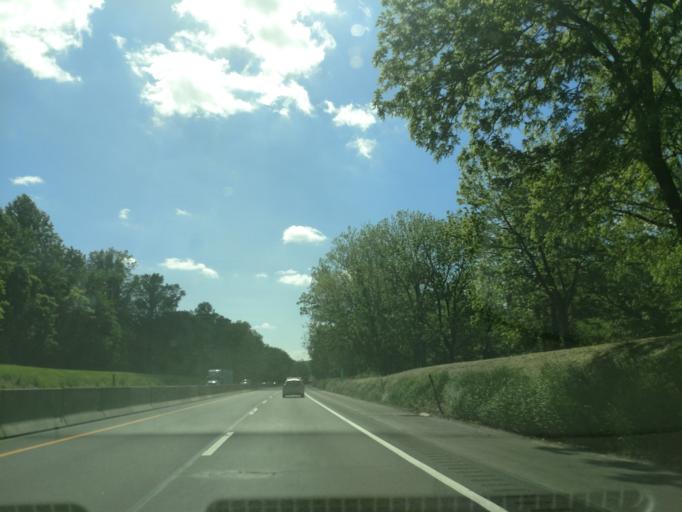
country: US
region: Pennsylvania
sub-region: Chester County
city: Chesterbrook
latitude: 40.0810
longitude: -75.4513
